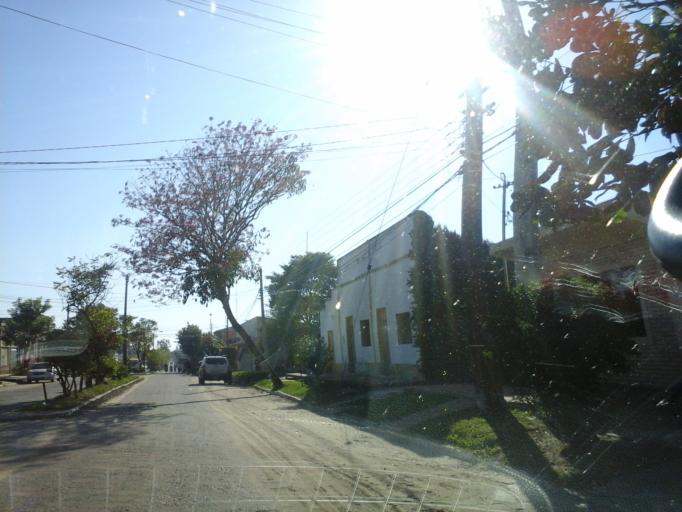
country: PY
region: Neembucu
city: Pilar
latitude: -26.8629
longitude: -58.3016
